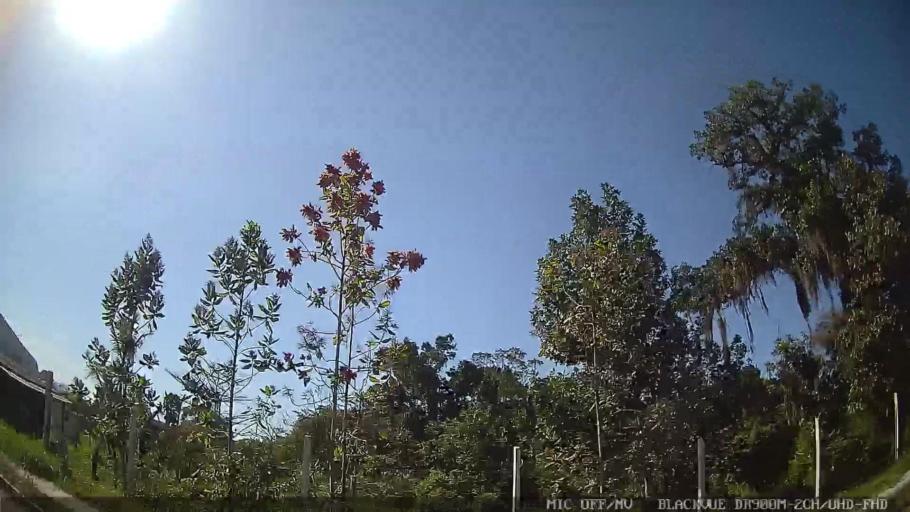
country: BR
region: Sao Paulo
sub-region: Guaruja
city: Guaruja
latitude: -23.9733
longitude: -46.2218
